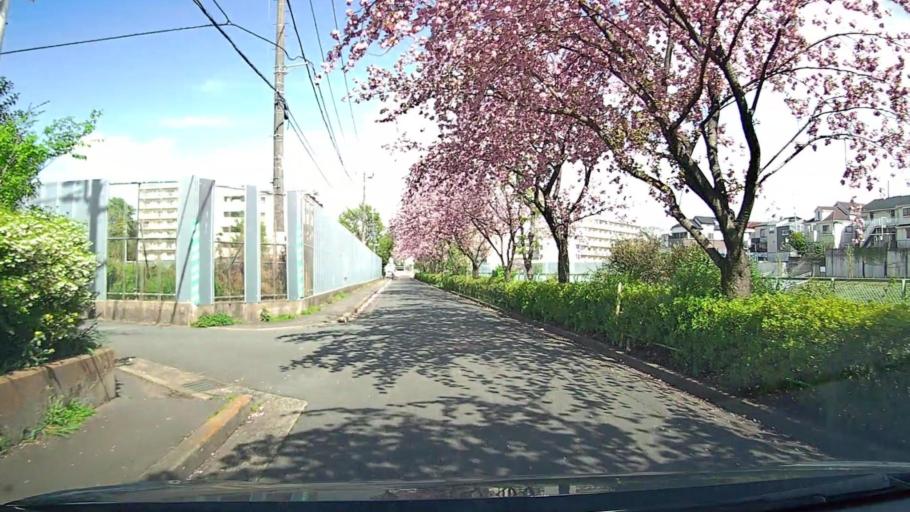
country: JP
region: Tokyo
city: Musashino
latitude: 35.7307
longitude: 139.5844
